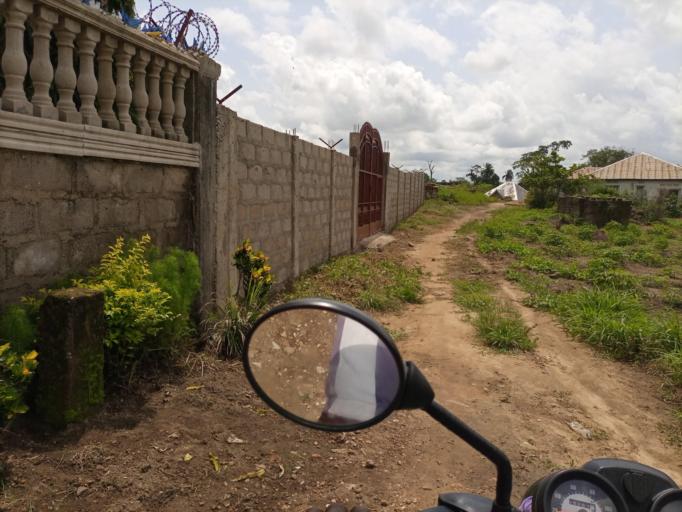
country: SL
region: Southern Province
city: Bo
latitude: 7.9802
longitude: -11.7682
